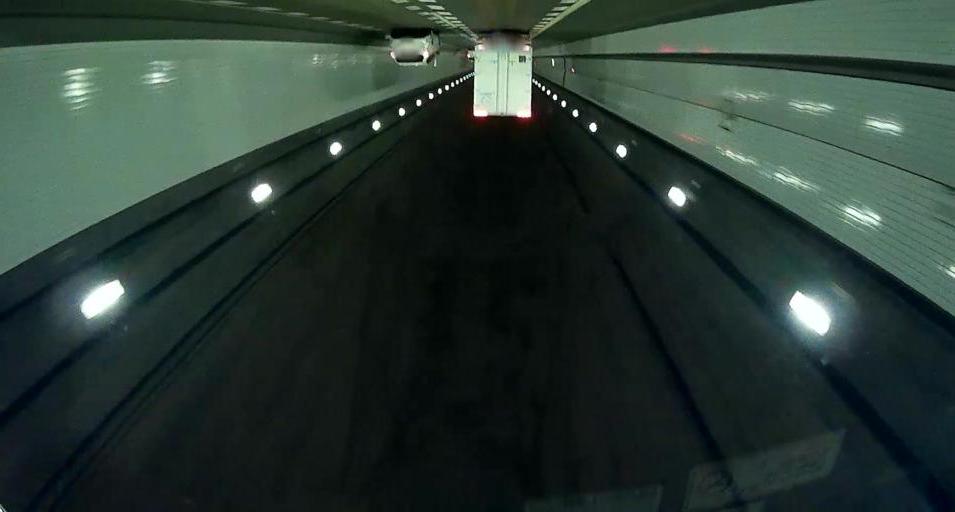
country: JP
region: Chiba
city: Kisarazu
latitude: 35.4663
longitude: 139.8711
